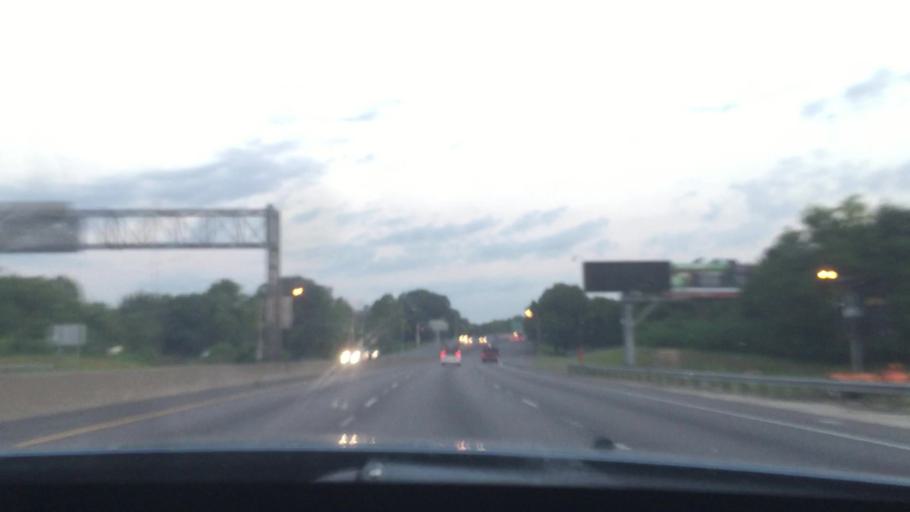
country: US
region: Louisiana
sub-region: East Baton Rouge Parish
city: Baton Rouge
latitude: 30.4281
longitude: -91.1705
